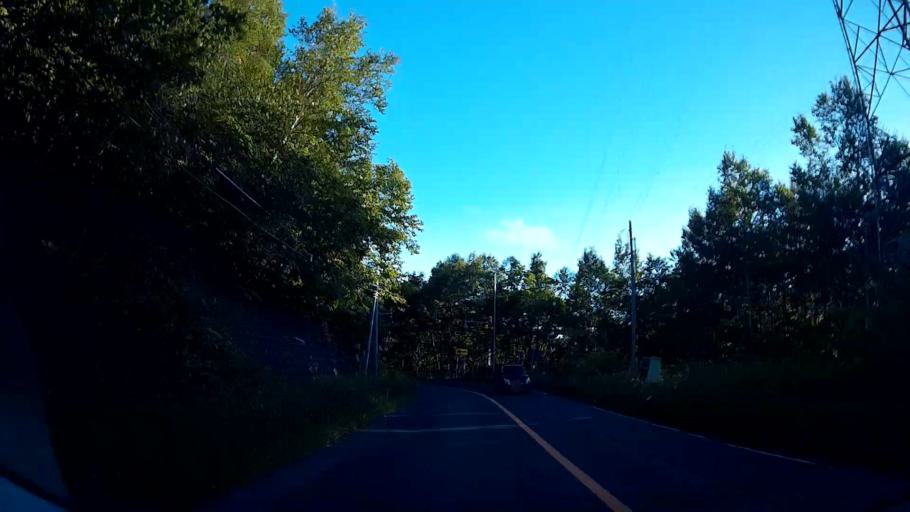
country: JP
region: Hokkaido
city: Otaru
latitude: 43.1671
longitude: 141.0024
